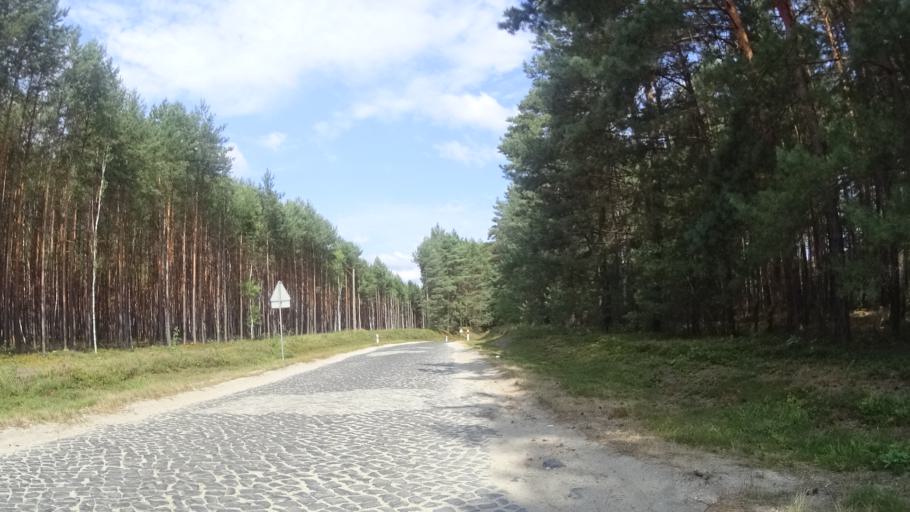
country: PL
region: Lubusz
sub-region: Powiat zarski
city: Leknica
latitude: 51.5225
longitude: 14.8239
